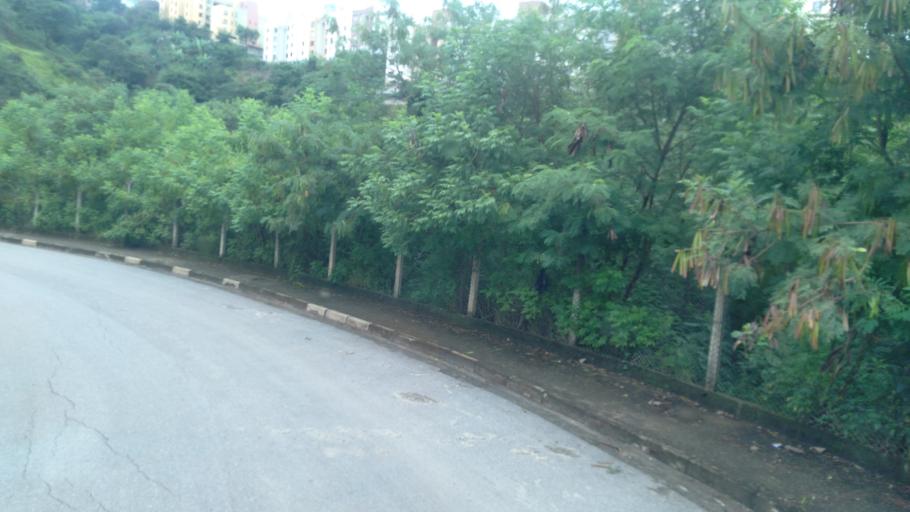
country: BR
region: Minas Gerais
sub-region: Belo Horizonte
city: Belo Horizonte
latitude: -19.9109
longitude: -43.8819
